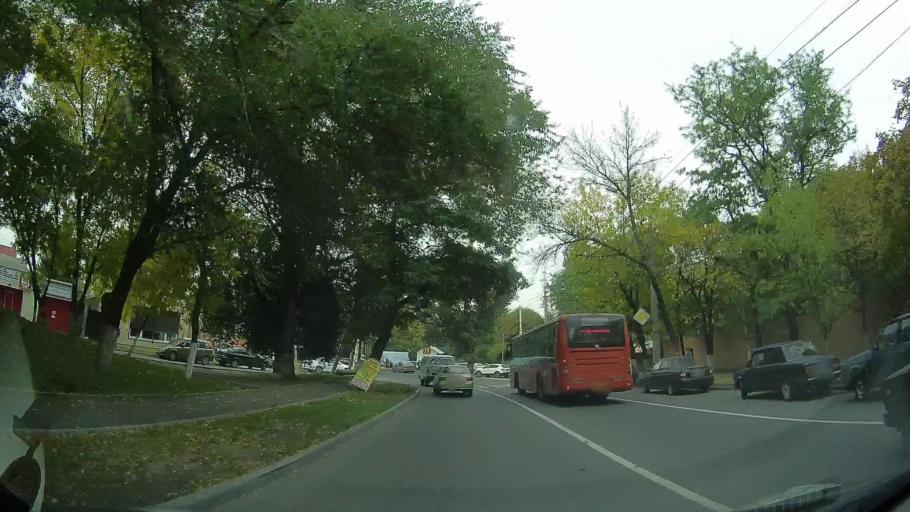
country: RU
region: Rostov
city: Severnyy
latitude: 47.2602
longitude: 39.6745
